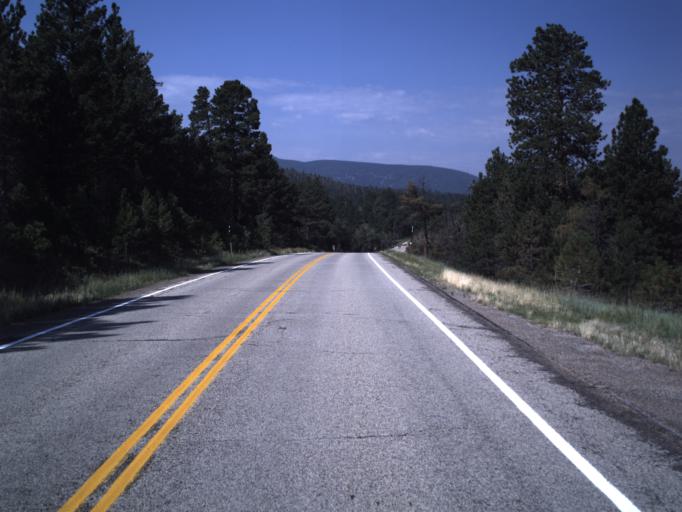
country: US
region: Utah
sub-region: Daggett County
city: Manila
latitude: 40.8639
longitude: -109.5233
